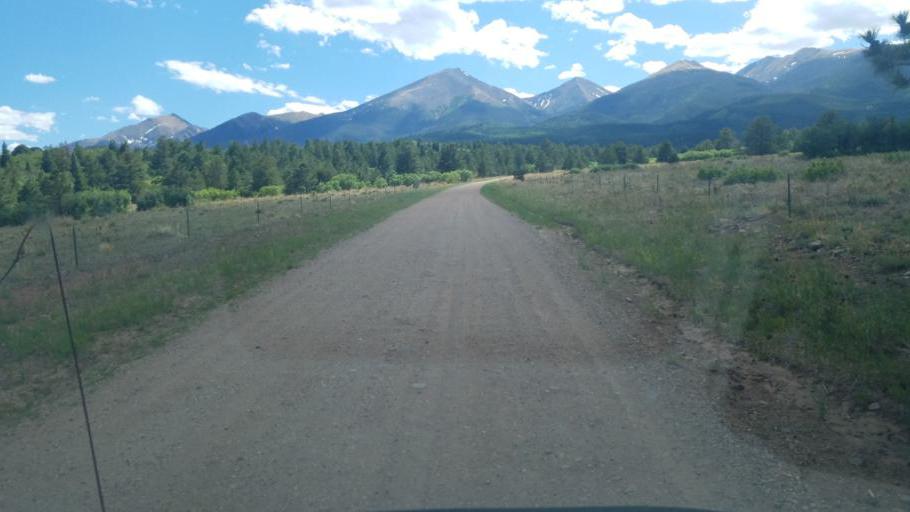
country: US
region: Colorado
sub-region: Custer County
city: Westcliffe
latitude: 38.2238
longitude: -105.6008
